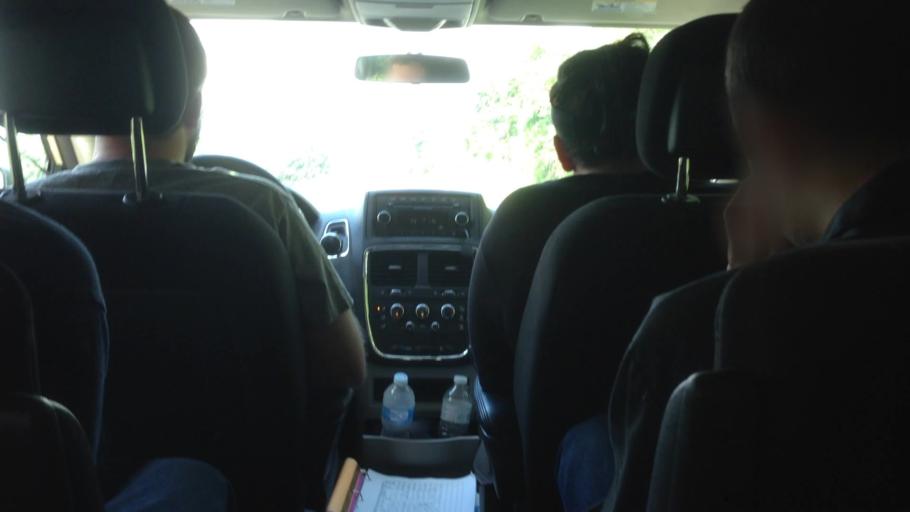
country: US
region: New York
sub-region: Dutchess County
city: Tivoli
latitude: 42.0864
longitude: -73.8955
